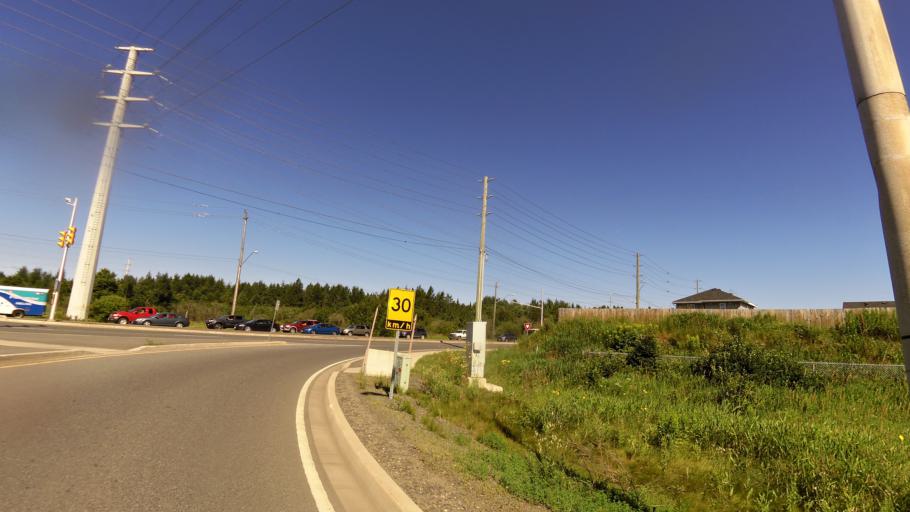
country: CA
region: Ontario
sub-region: Thunder Bay District
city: Thunder Bay
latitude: 48.4057
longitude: -89.2739
